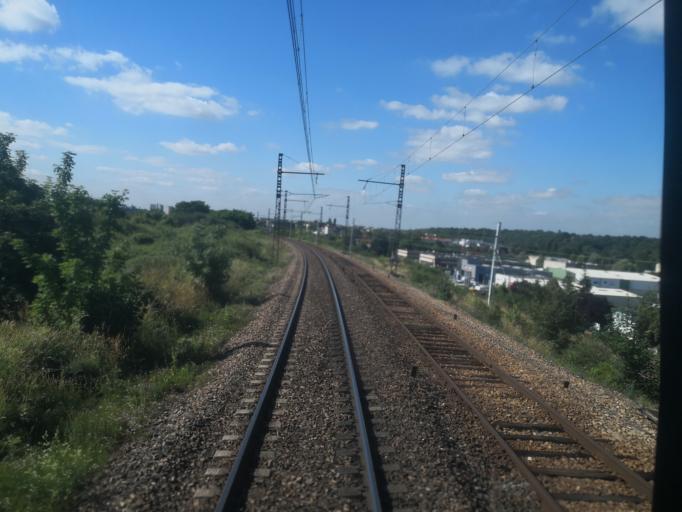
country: FR
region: Ile-de-France
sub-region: Departement de Seine-et-Marne
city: La Rochette
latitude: 48.5203
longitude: 2.6657
